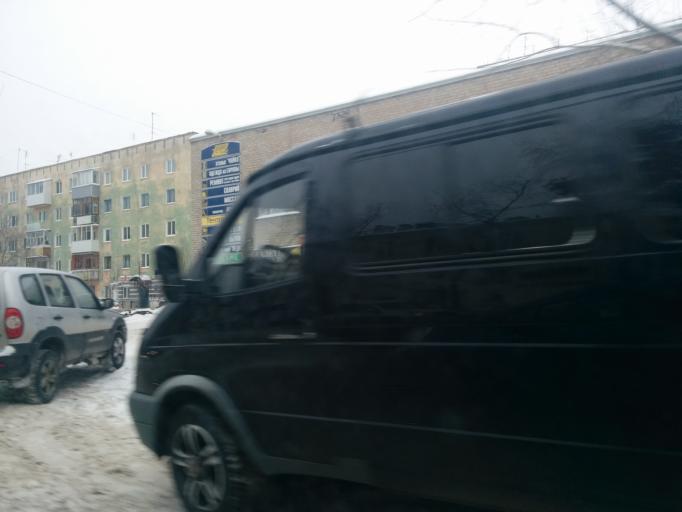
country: RU
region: Perm
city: Kondratovo
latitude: 58.0273
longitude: 56.0161
